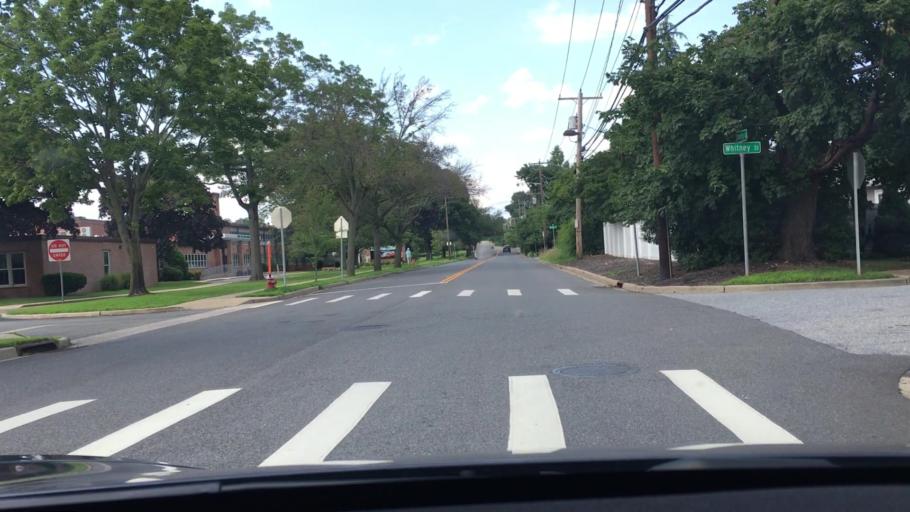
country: US
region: New York
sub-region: Nassau County
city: Carle Place
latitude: 40.7546
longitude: -73.6052
